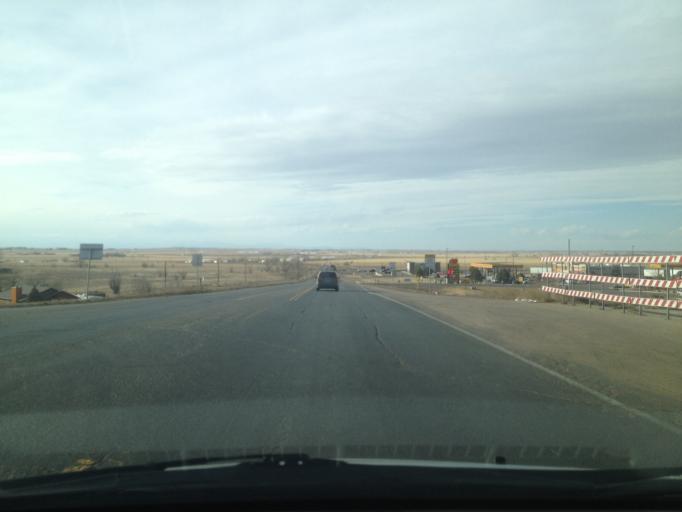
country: US
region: Colorado
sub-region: Weld County
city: Hudson
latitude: 40.0753
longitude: -104.6476
